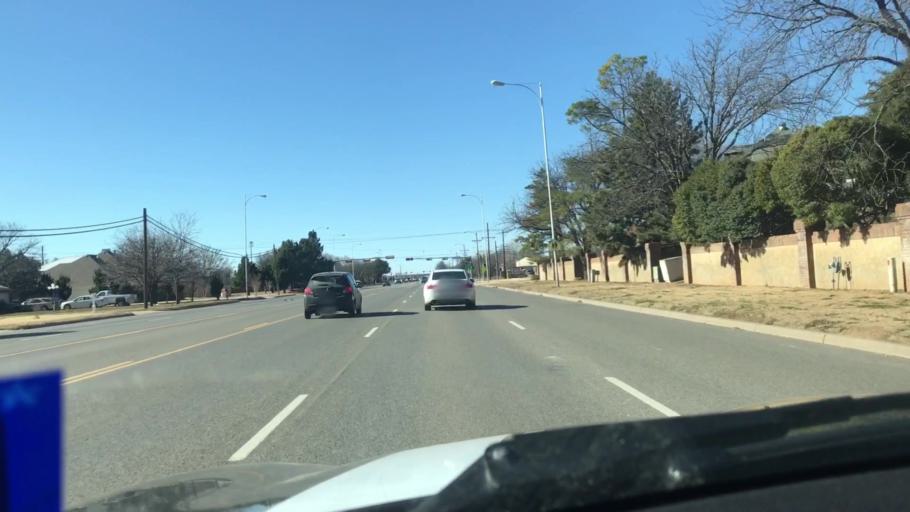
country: US
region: Texas
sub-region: Lubbock County
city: Lubbock
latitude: 33.5779
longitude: -101.9292
